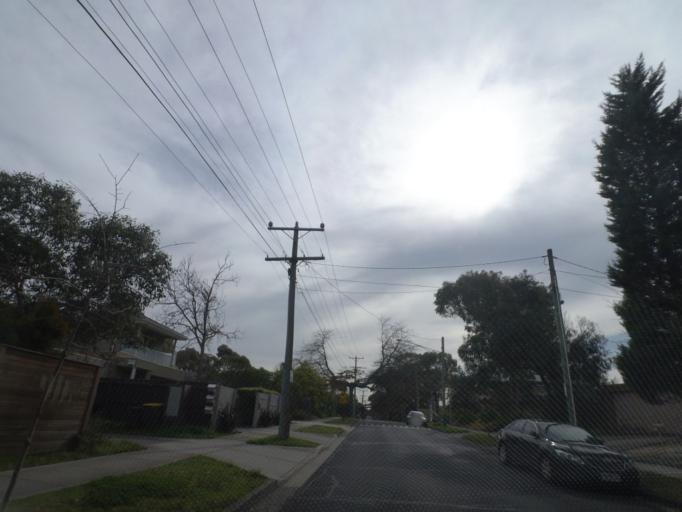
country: AU
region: Victoria
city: Mitcham
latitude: -37.8200
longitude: 145.2084
